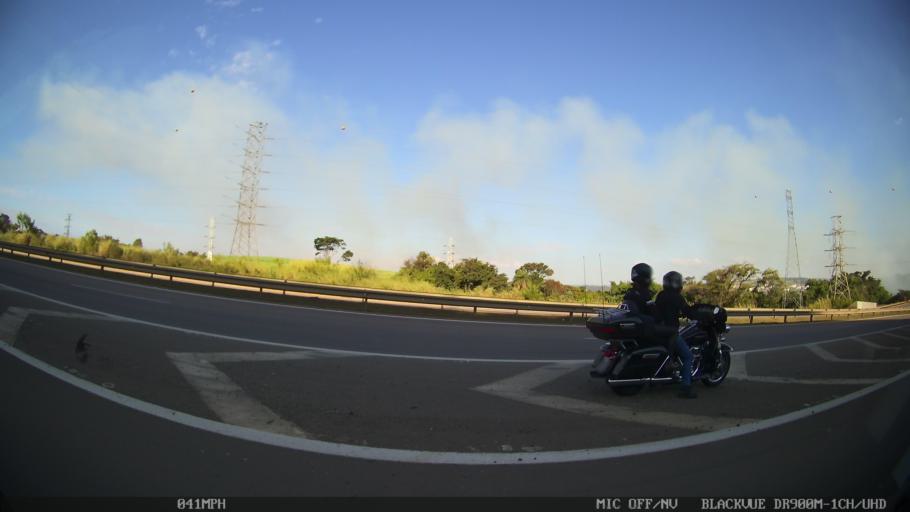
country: BR
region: Sao Paulo
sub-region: Piracicaba
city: Piracicaba
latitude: -22.6891
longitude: -47.5990
